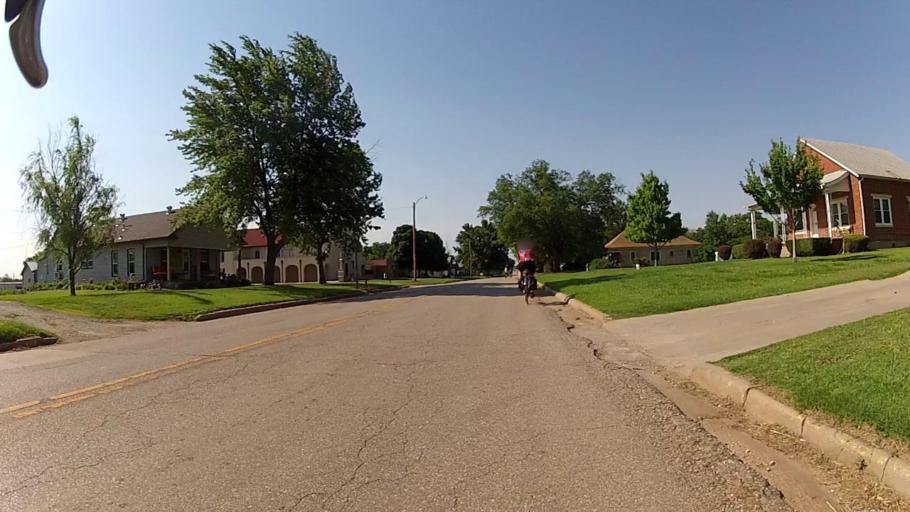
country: US
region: Kansas
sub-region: Sumner County
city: Caldwell
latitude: 37.0386
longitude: -97.6069
